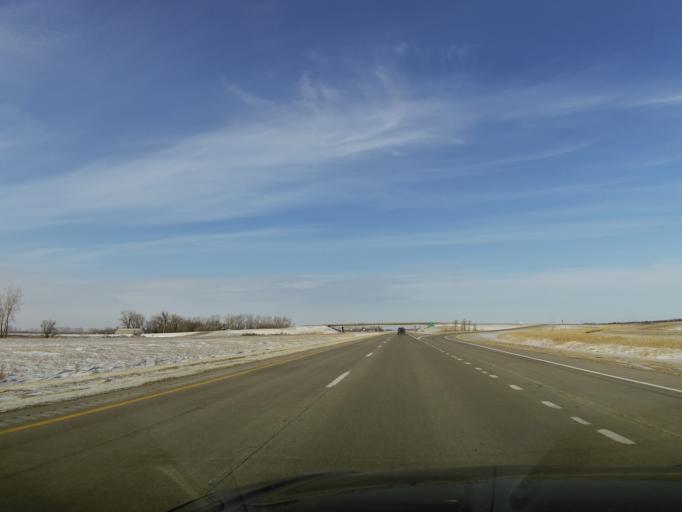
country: US
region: North Dakota
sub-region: Walsh County
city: Grafton
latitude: 48.4669
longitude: -97.1902
